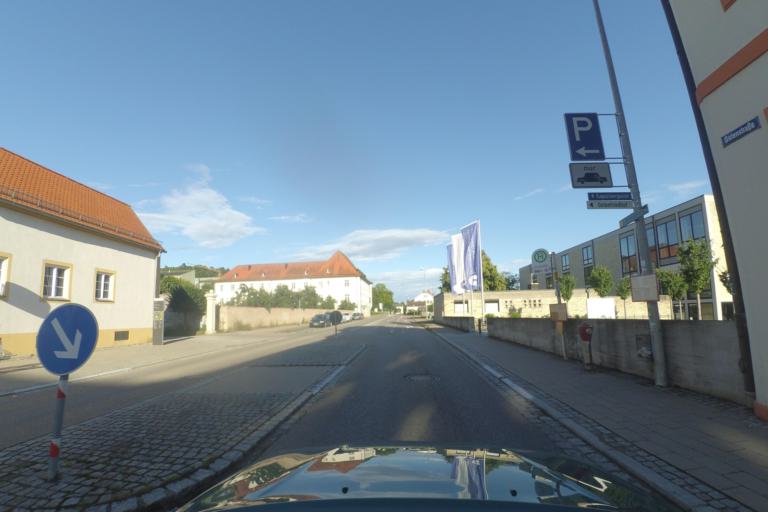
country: DE
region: Bavaria
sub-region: Upper Bavaria
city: Eichstaett
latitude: 48.8897
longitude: 11.1899
